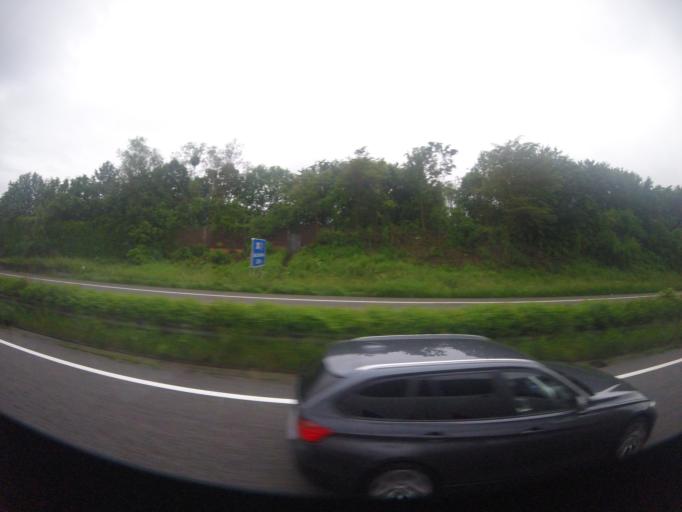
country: DE
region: Saarland
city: Eppelborn
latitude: 49.3529
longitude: 6.9841
